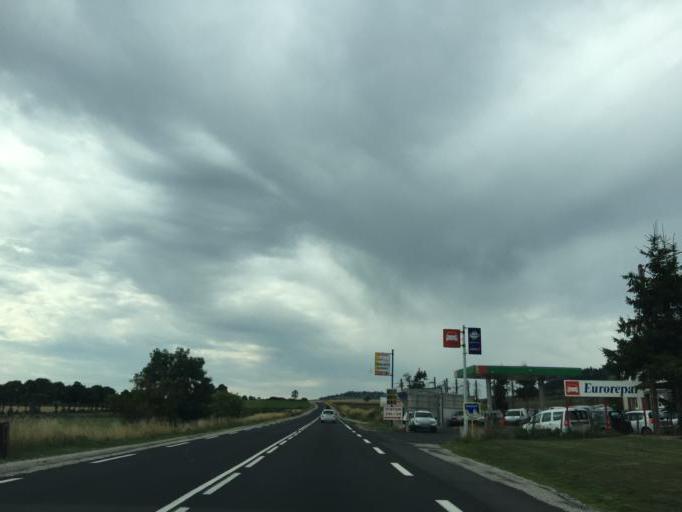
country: FR
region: Auvergne
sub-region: Departement de la Haute-Loire
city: Solignac-sur-Loire
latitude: 44.8889
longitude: 3.8479
